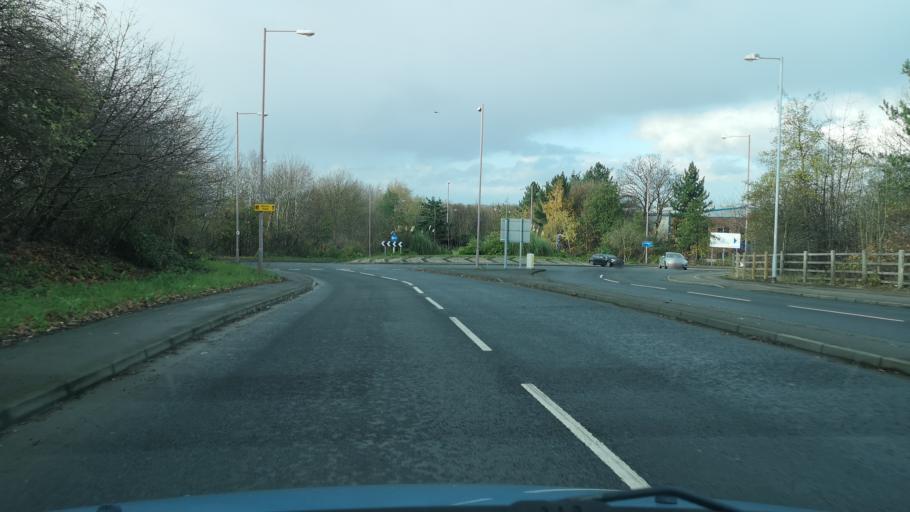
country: GB
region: England
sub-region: City and Borough of Wakefield
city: Normanton
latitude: 53.7004
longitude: -1.3926
